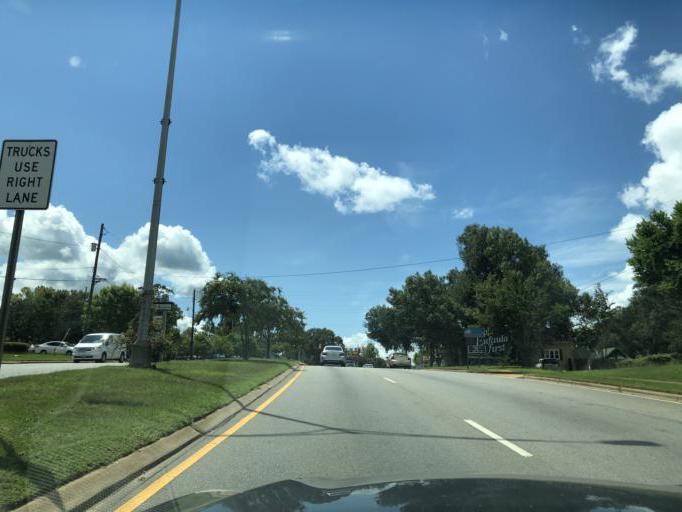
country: US
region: Alabama
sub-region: Barbour County
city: Eufaula
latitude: 31.8894
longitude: -85.1456
